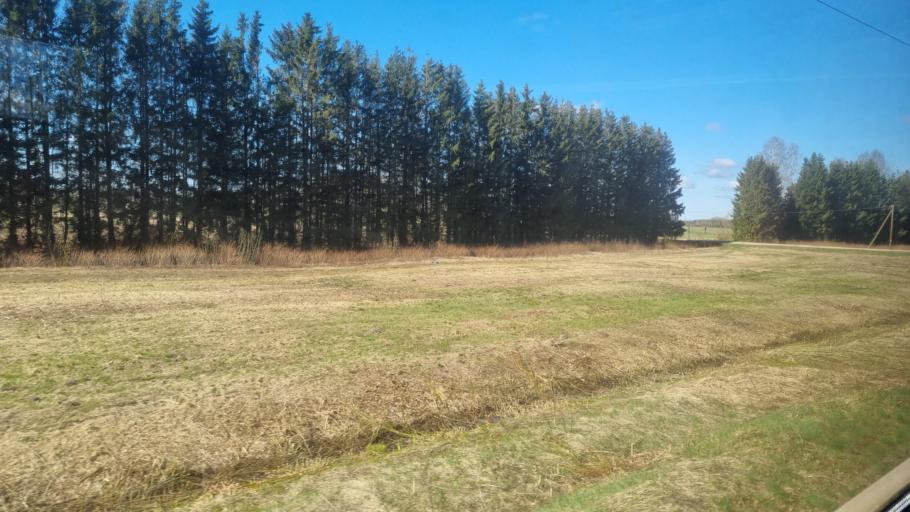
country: LV
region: Ogre
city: Jumprava
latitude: 56.6712
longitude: 24.9987
